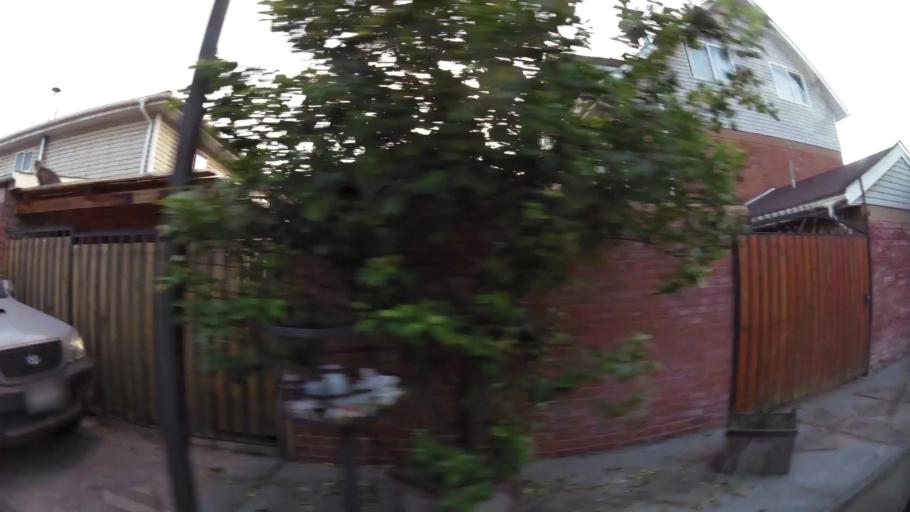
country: CL
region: Santiago Metropolitan
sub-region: Provincia de Cordillera
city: Puente Alto
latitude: -33.5987
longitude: -70.5871
